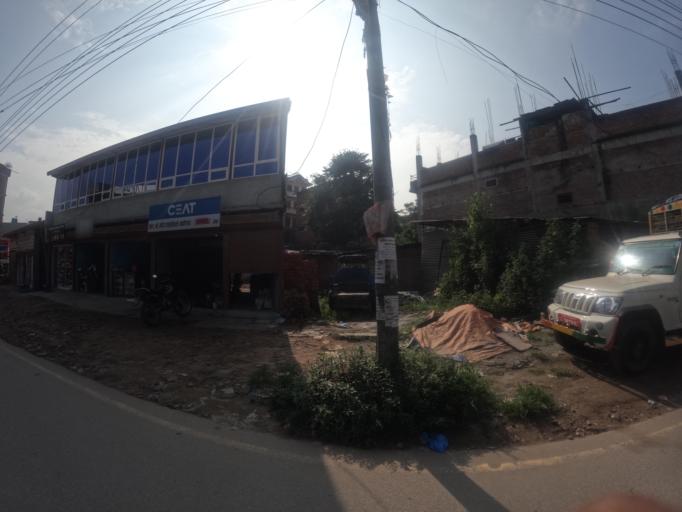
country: NP
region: Central Region
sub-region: Bagmati Zone
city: Bhaktapur
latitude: 27.6769
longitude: 85.4330
